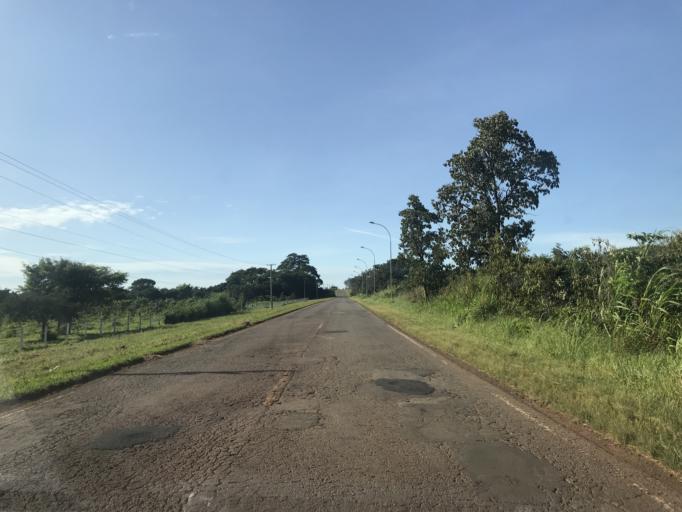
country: BR
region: Federal District
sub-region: Brasilia
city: Brasilia
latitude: -15.9253
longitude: -48.1438
